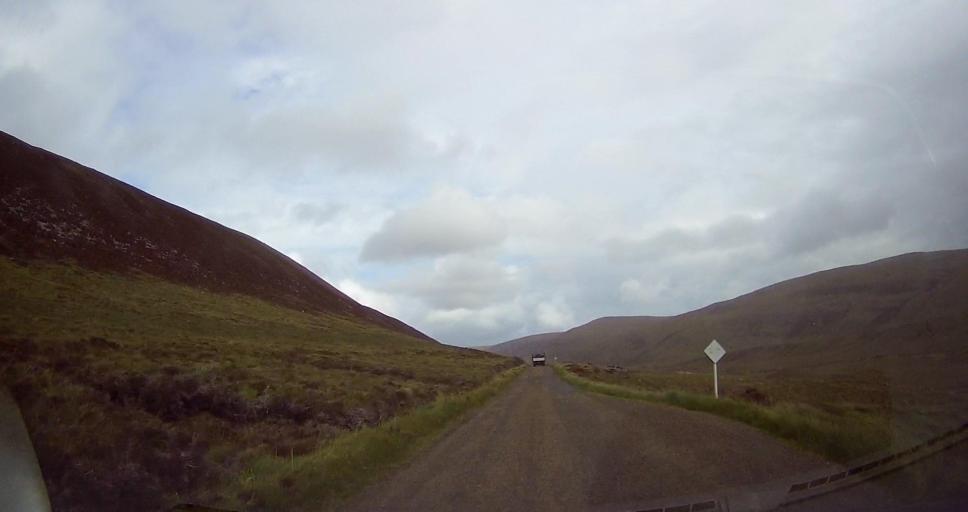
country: GB
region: Scotland
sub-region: Orkney Islands
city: Stromness
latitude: 58.8817
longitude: -3.3665
